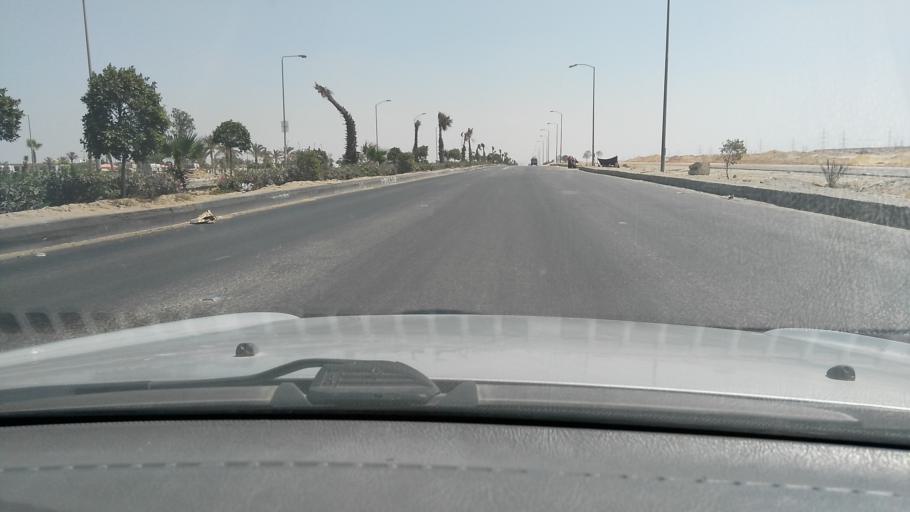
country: EG
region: Al Jizah
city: Madinat Sittah Uktubar
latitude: 29.9540
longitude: 30.9575
